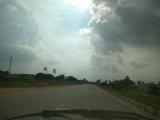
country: IN
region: Karnataka
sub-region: Bangalore Rural
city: Dasarahalli
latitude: 13.1337
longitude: 77.9463
